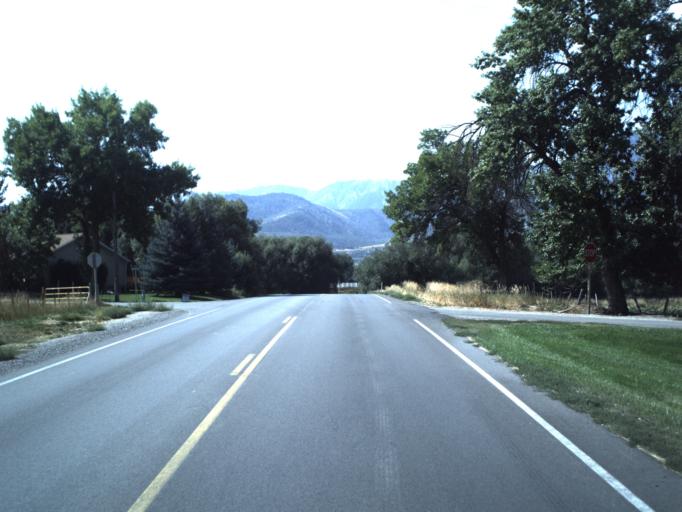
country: US
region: Utah
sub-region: Cache County
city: Wellsville
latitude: 41.6406
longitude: -111.9216
